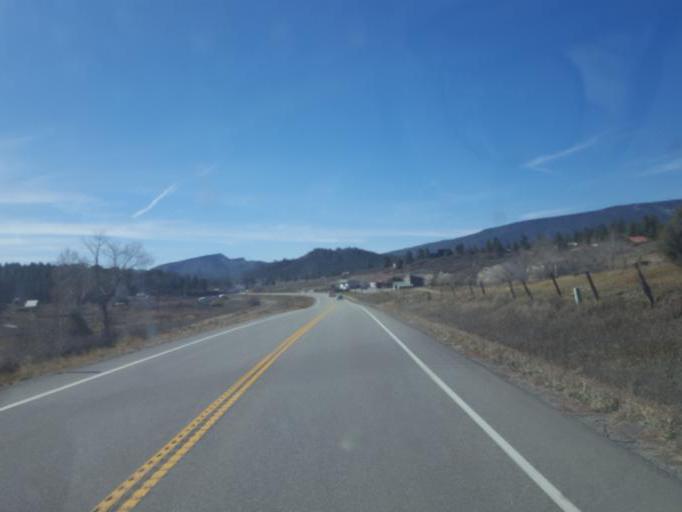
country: US
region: Colorado
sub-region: Archuleta County
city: Pagosa Springs
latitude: 37.2381
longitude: -107.1623
